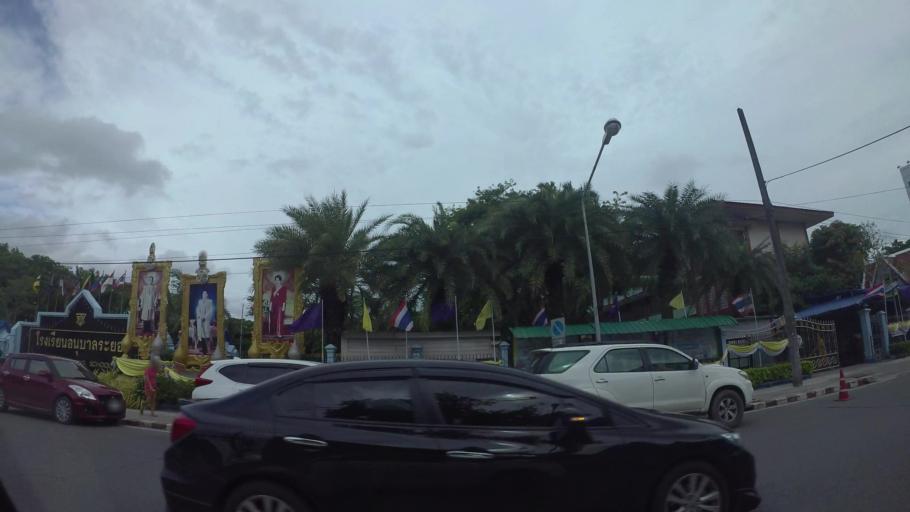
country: TH
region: Rayong
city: Rayong
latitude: 12.6750
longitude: 101.2787
